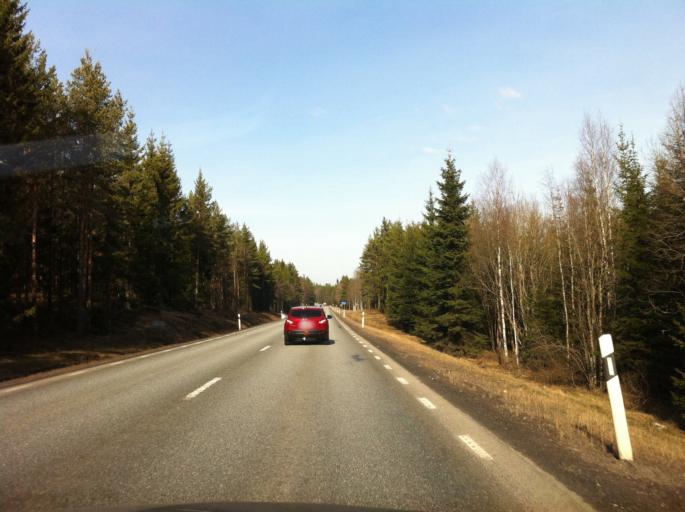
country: SE
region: Joenkoeping
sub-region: Mullsjo Kommun
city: Mullsjoe
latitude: 58.0020
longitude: 13.8301
